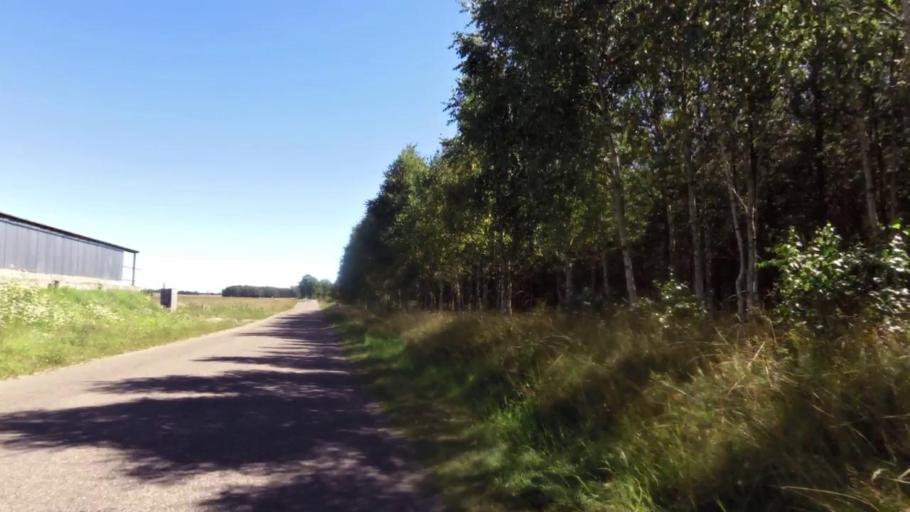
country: PL
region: West Pomeranian Voivodeship
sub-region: Powiat szczecinecki
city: Bialy Bor
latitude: 53.8942
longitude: 16.8542
